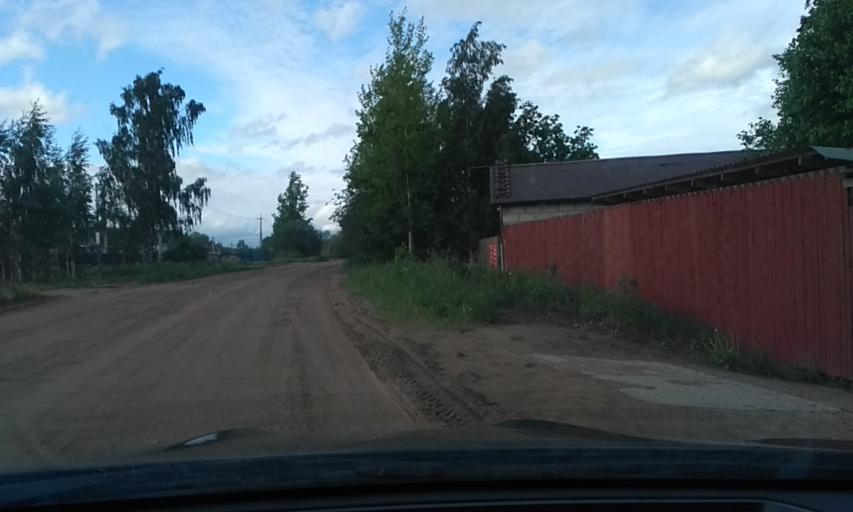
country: RU
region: Leningrad
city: Otradnoye
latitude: 59.7969
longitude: 30.7988
